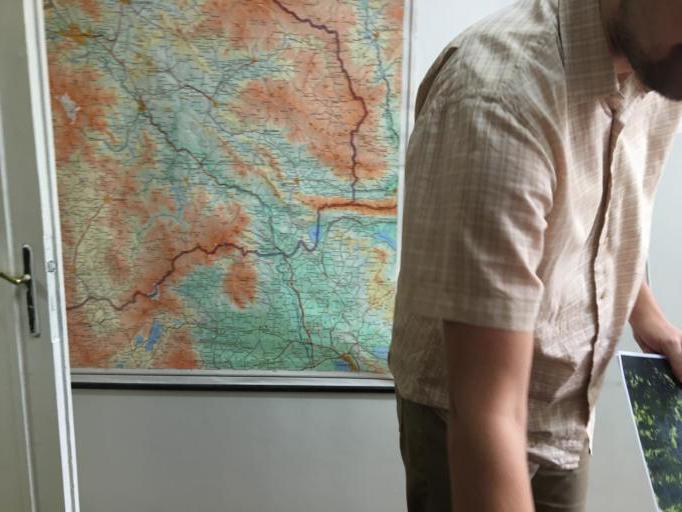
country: MK
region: Cair
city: Cair
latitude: 42.0030
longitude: 21.4501
